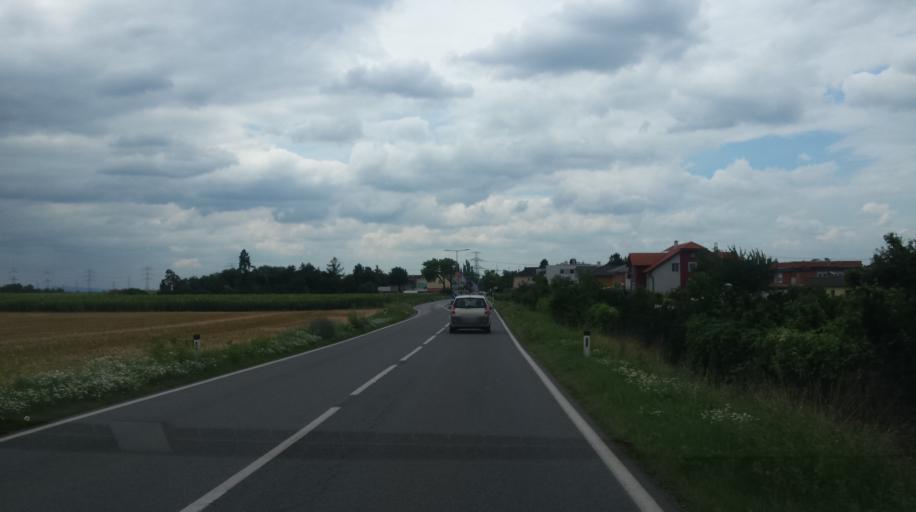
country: AT
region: Lower Austria
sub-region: Politischer Bezirk Wien-Umgebung
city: Zwolfaxing
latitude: 48.1017
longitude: 16.4571
